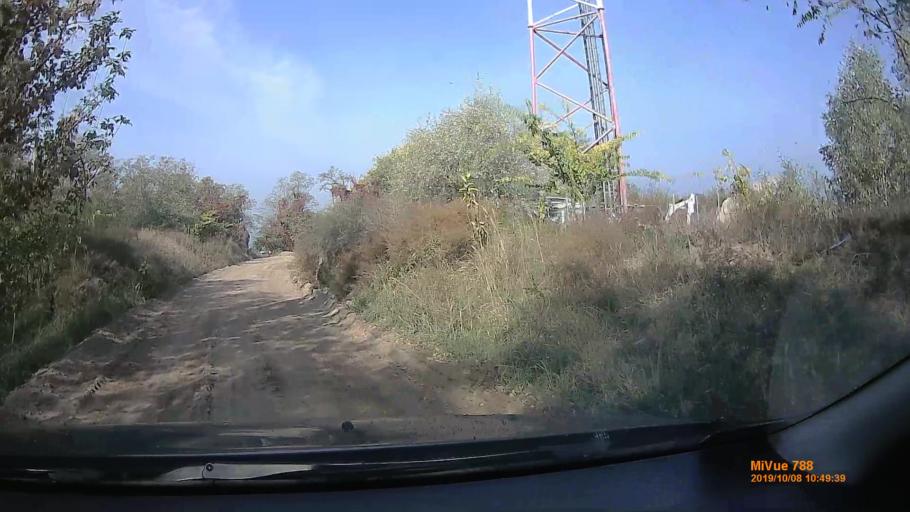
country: HU
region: Pest
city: Dunakeszi
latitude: 47.6576
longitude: 19.1566
